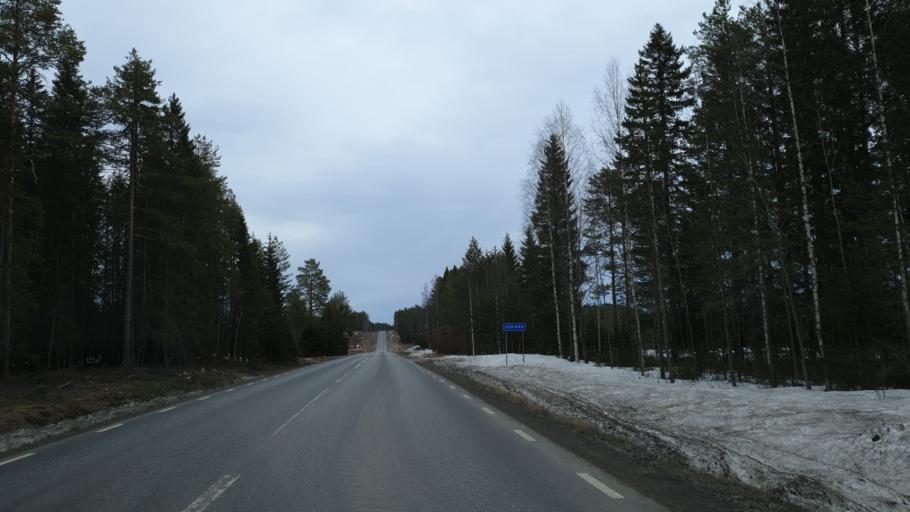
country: SE
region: Vaesterbotten
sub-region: Robertsfors Kommun
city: Robertsfors
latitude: 64.2169
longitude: 20.8985
